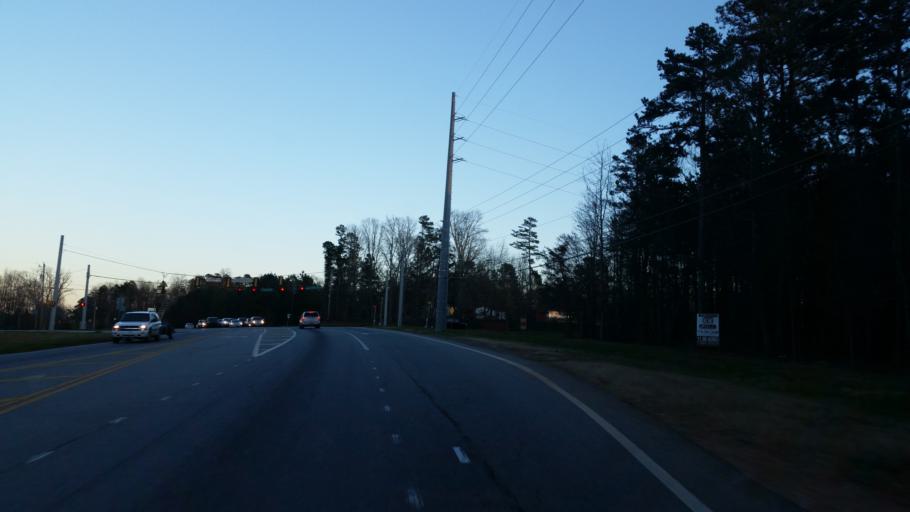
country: US
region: Georgia
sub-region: Hall County
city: Oakwood
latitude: 34.3044
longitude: -83.9800
